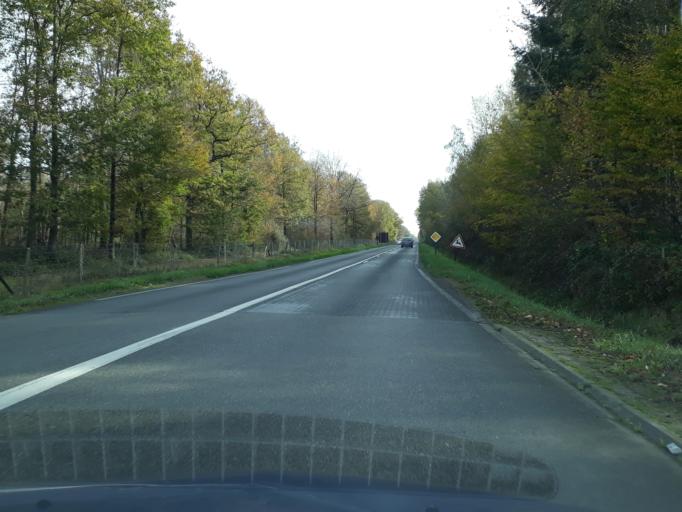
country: FR
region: Ile-de-France
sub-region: Departement de Seine-et-Marne
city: Vernou-la-Celle-sur-Seine
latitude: 48.4188
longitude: 2.8487
